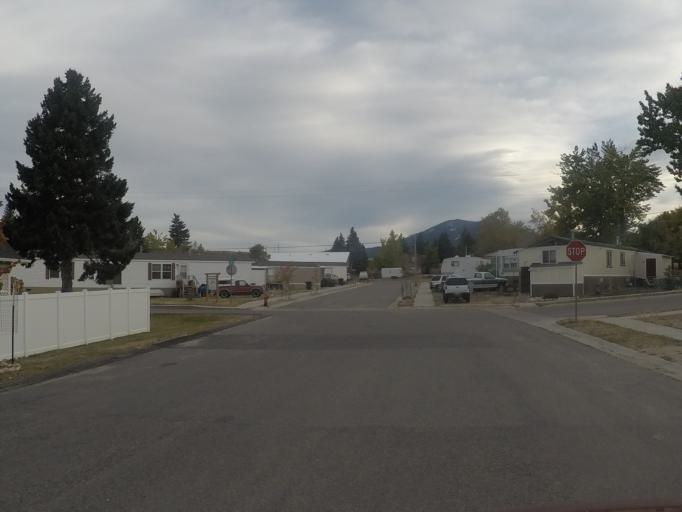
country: US
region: Montana
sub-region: Carbon County
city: Red Lodge
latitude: 45.1969
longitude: -109.2481
